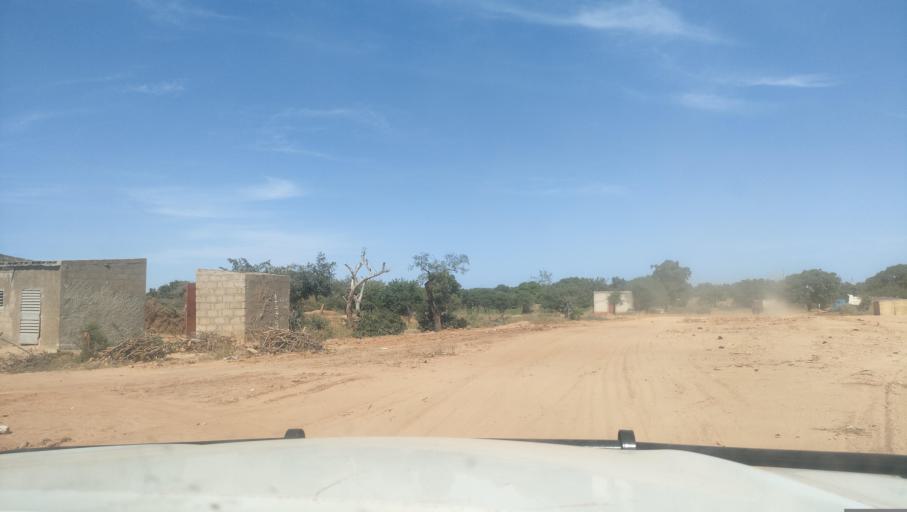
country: BF
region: Est
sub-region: Province du Gourma
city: Fada N'gourma
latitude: 12.0704
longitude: 0.3362
